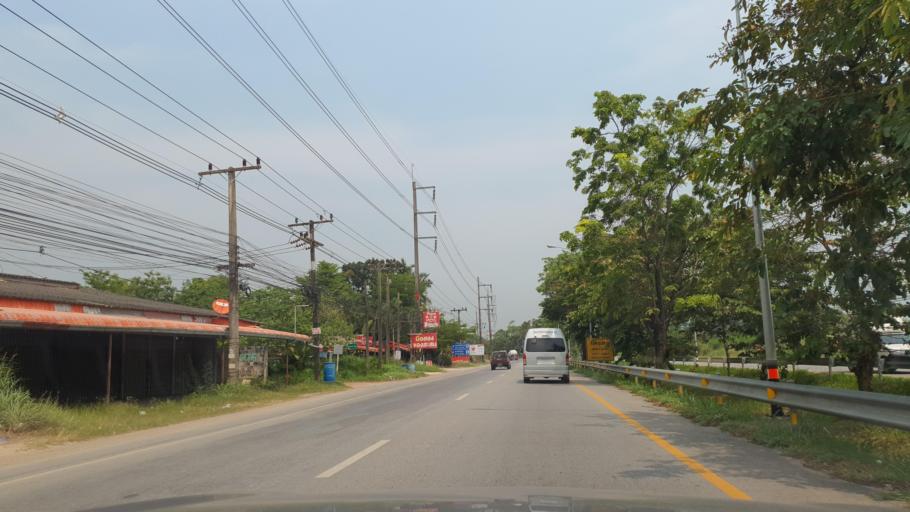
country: TH
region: Rayong
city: Rayong
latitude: 12.6407
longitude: 101.3610
